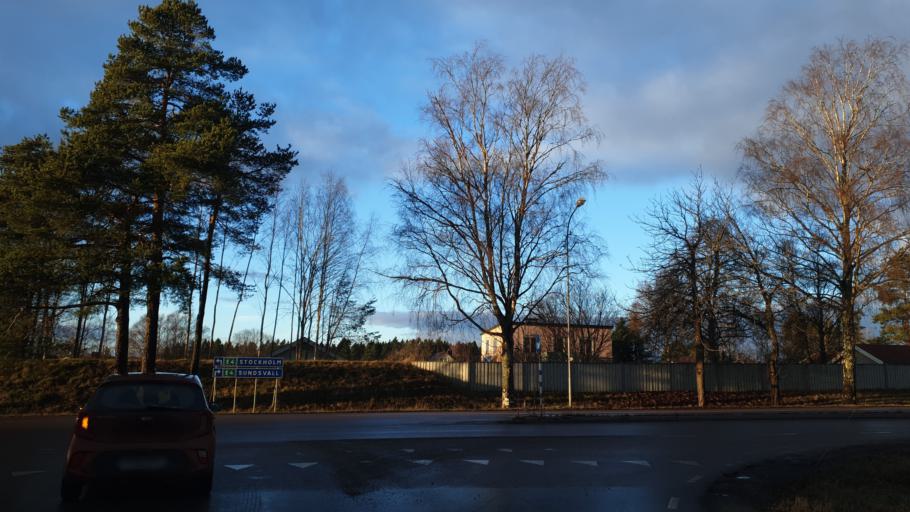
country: SE
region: Gaevleborg
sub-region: Hudiksvalls Kommun
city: Hudiksvall
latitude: 61.7518
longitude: 17.1206
